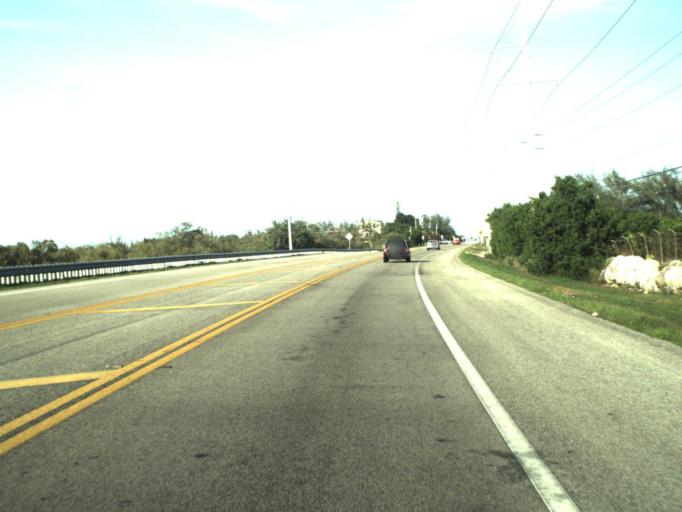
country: US
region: Florida
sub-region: Monroe County
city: Marathon
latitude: 24.7717
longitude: -80.9380
